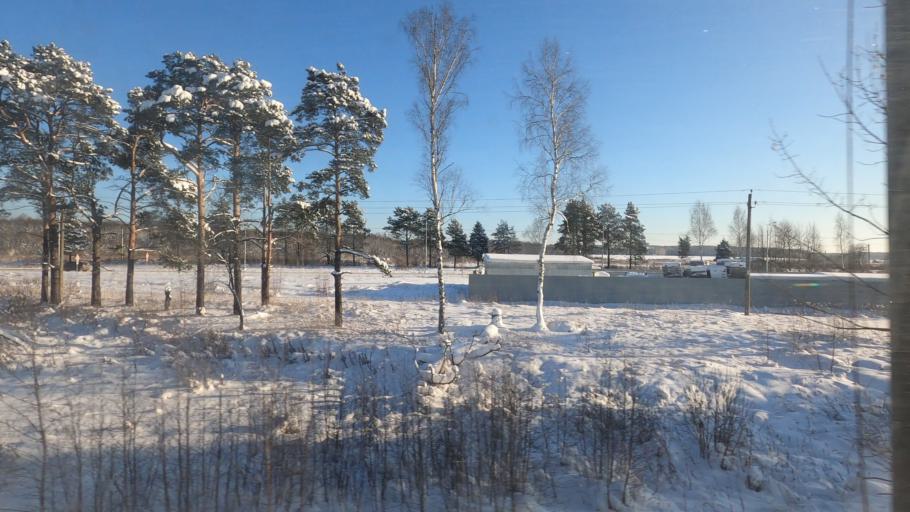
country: RU
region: Moskovskaya
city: Orud'yevo
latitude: 56.4510
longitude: 37.5254
